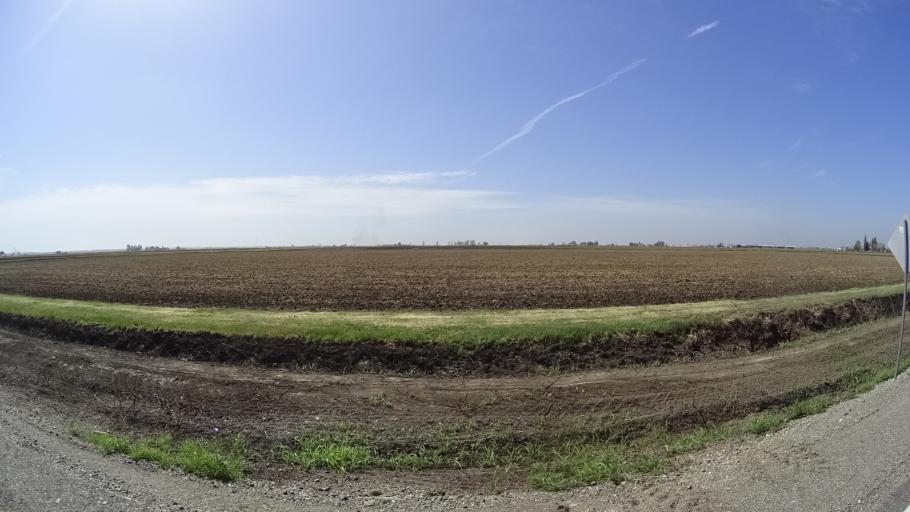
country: US
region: California
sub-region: Glenn County
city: Willows
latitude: 39.5826
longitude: -122.0576
